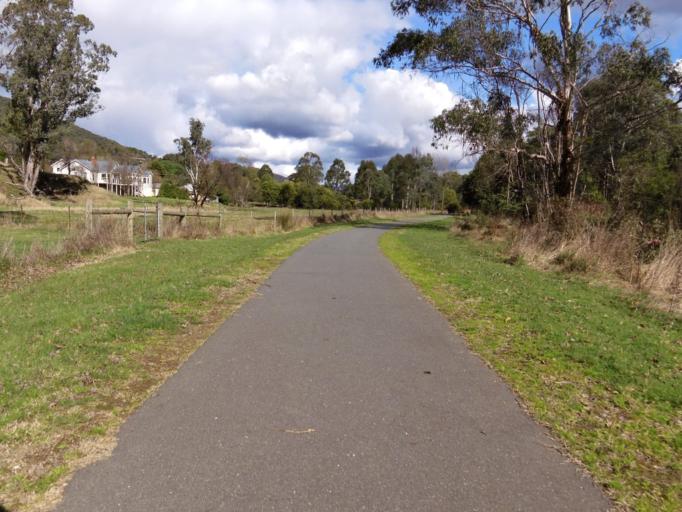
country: AU
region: Victoria
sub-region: Alpine
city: Mount Beauty
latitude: -36.7614
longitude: 146.9817
